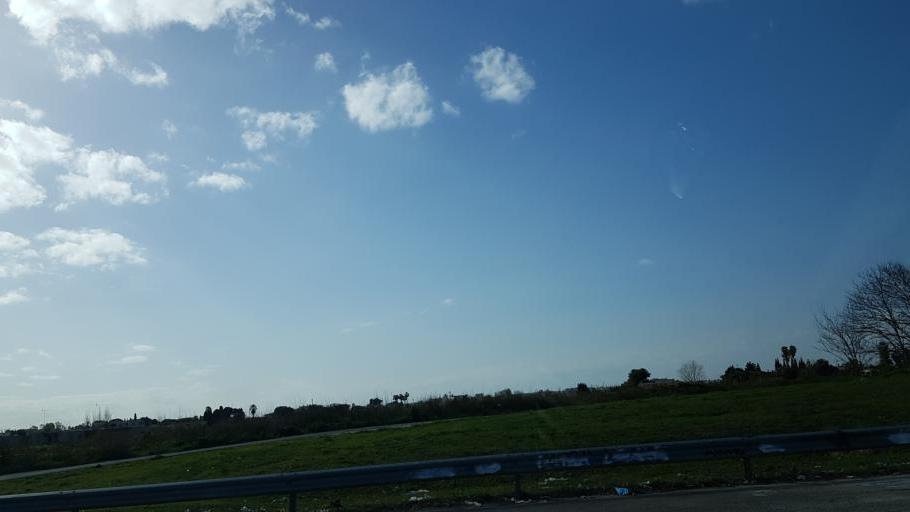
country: IT
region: Apulia
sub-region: Provincia di Brindisi
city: Brindisi
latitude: 40.6500
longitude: 17.9362
